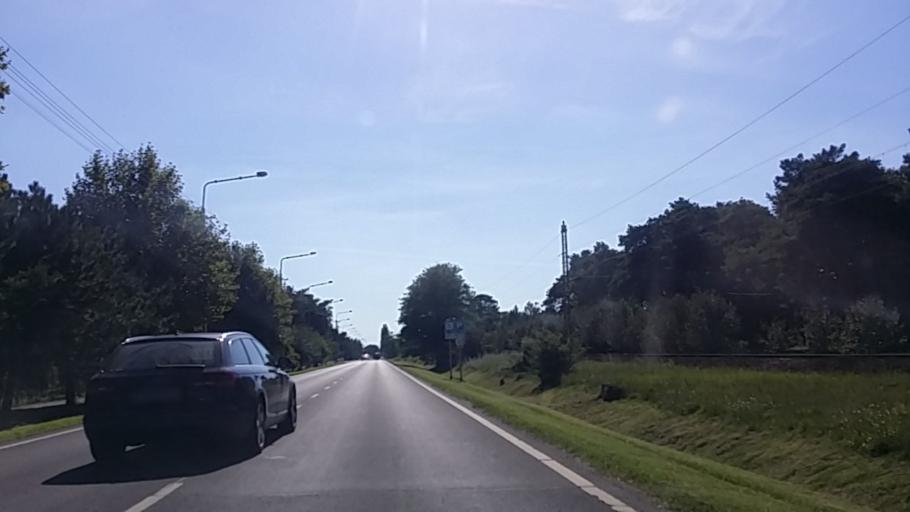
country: HU
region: Somogy
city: Balatonfenyves
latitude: 46.7197
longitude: 17.5053
